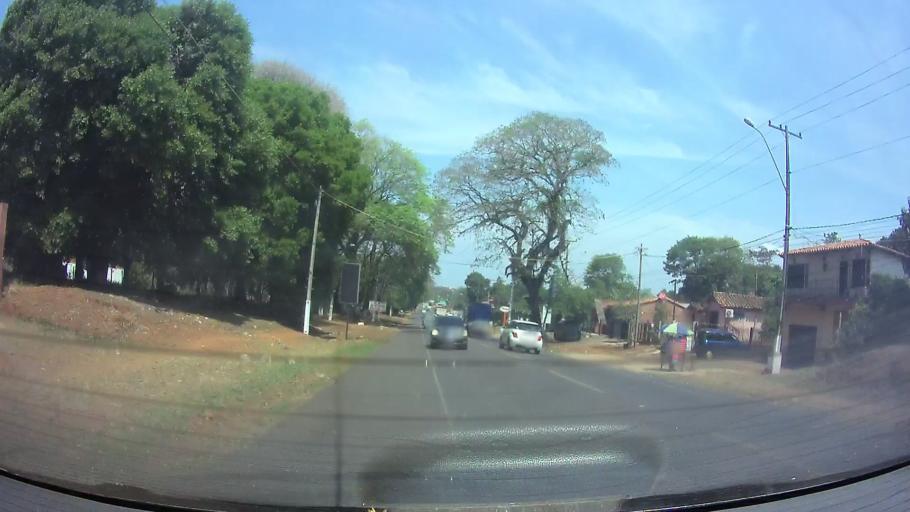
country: PY
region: Central
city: Capiata
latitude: -25.4123
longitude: -57.4586
